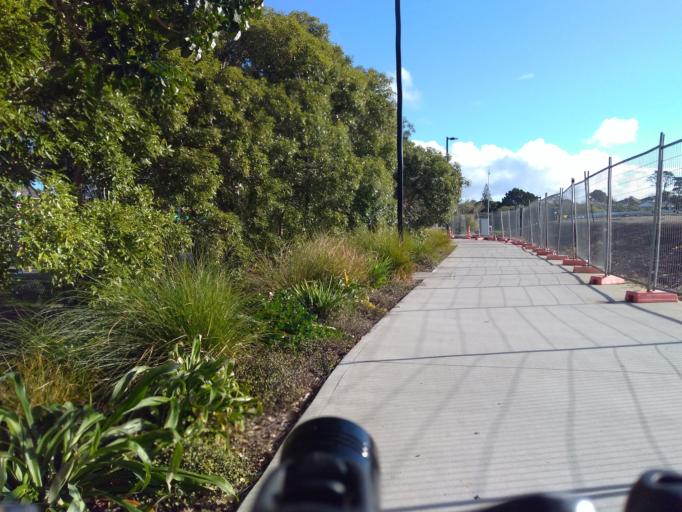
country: NZ
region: Auckland
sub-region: Auckland
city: Rosebank
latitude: -36.8847
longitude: 174.7048
